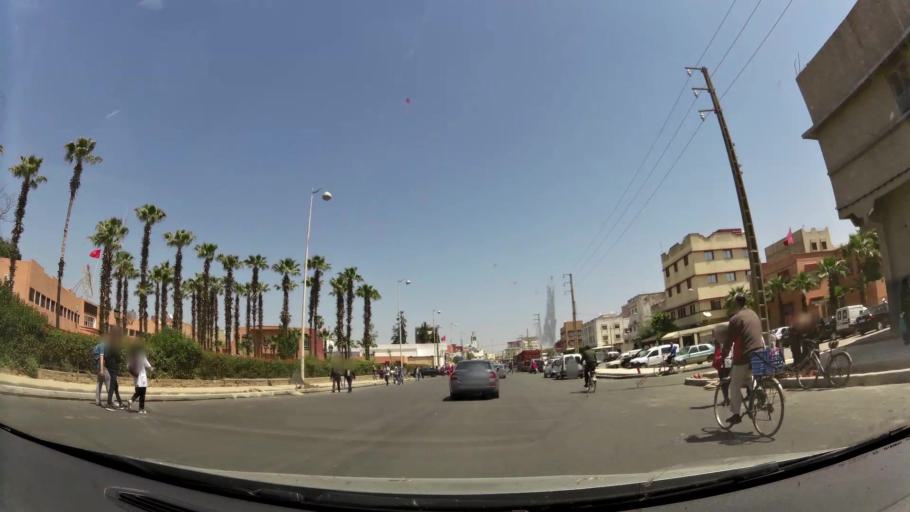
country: MA
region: Rabat-Sale-Zemmour-Zaer
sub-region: Khemisset
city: Khemisset
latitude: 33.8235
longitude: -6.0717
